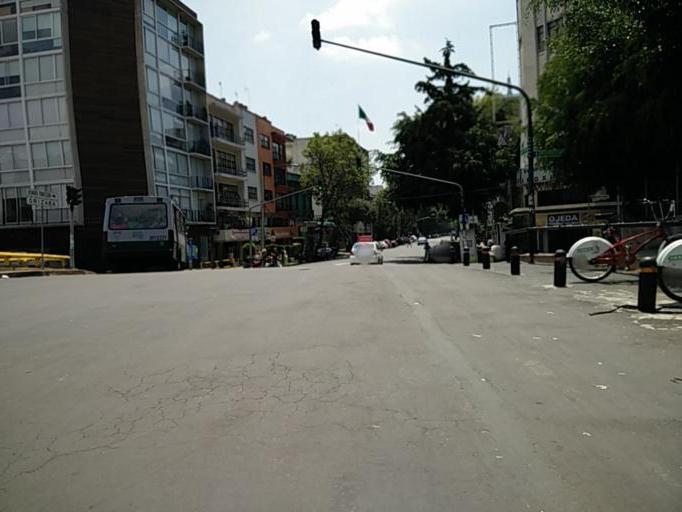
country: MX
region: Mexico City
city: Cuauhtemoc
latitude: 19.4242
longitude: -99.1613
